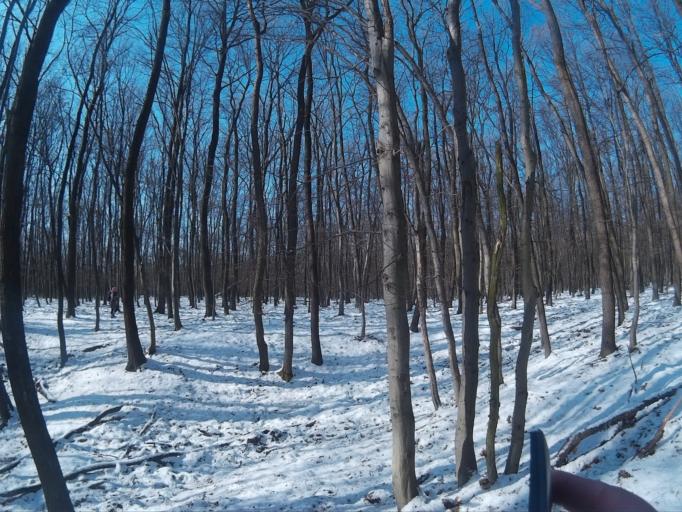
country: HU
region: Komarom-Esztergom
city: Labatlan
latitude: 47.6954
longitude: 18.5186
